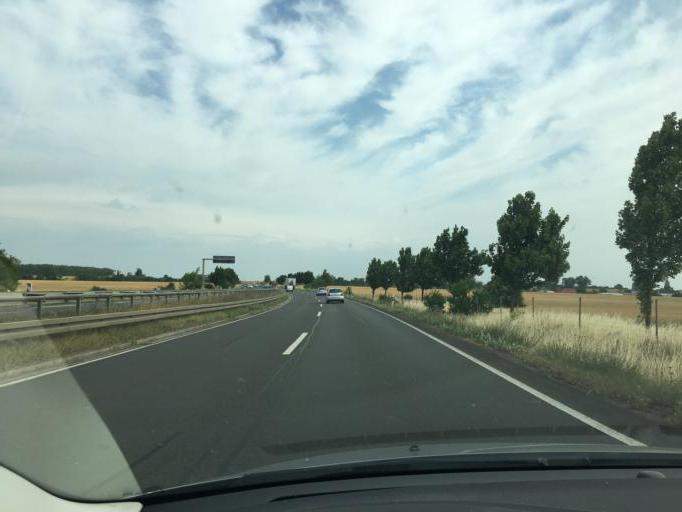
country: DE
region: Saxony-Anhalt
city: Barleben
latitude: 52.2213
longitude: 11.6067
